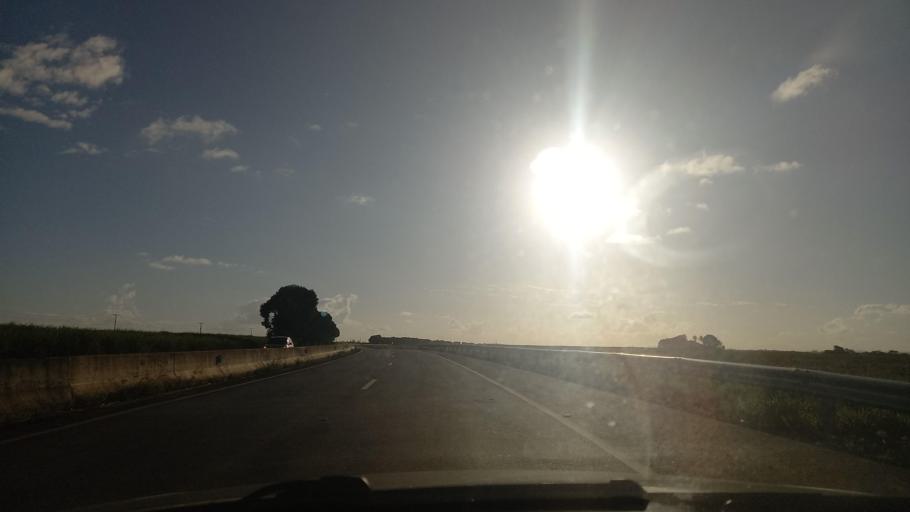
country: BR
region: Alagoas
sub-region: Campo Alegre
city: Campo Alegre
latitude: -9.8012
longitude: -36.2793
